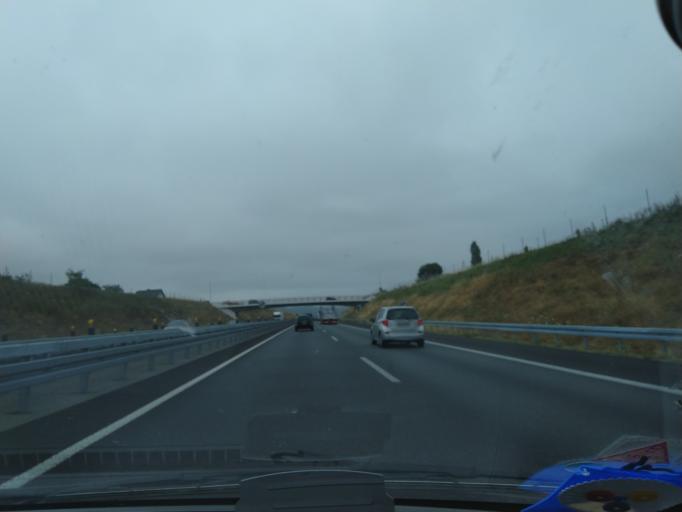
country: DE
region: North Rhine-Westphalia
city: Bad Oeynhausen
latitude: 52.2248
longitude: 8.7673
